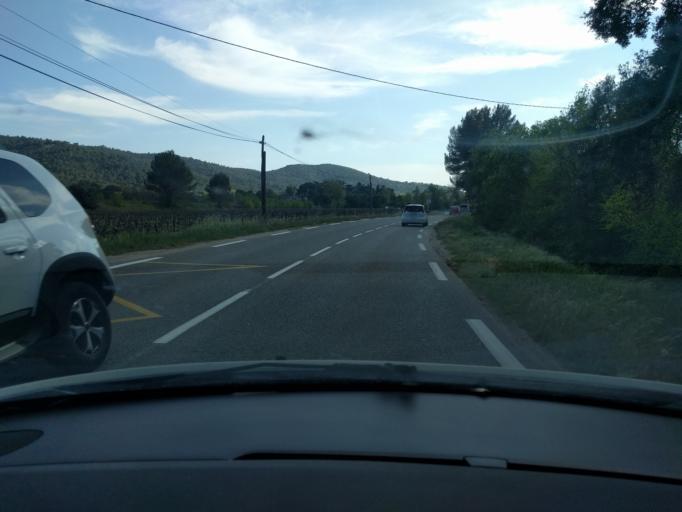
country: FR
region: Provence-Alpes-Cote d'Azur
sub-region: Departement du Var
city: Pierrefeu-du-Var
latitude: 43.2028
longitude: 6.1354
